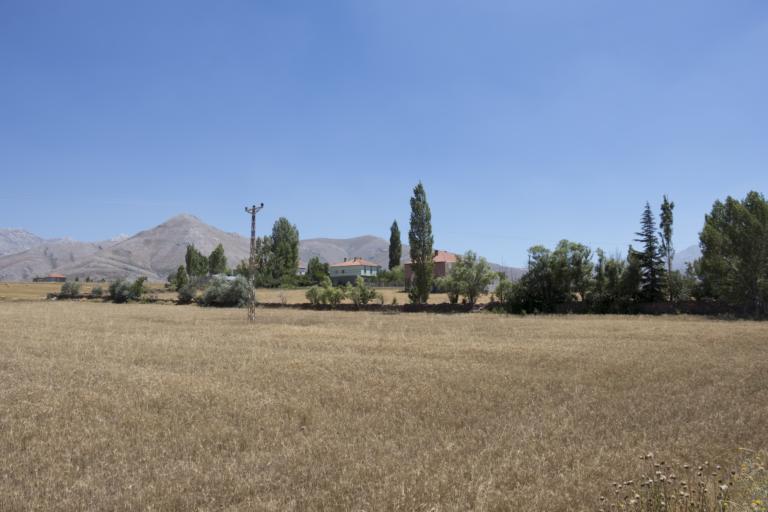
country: TR
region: Kayseri
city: Toklar
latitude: 38.4124
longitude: 36.0782
